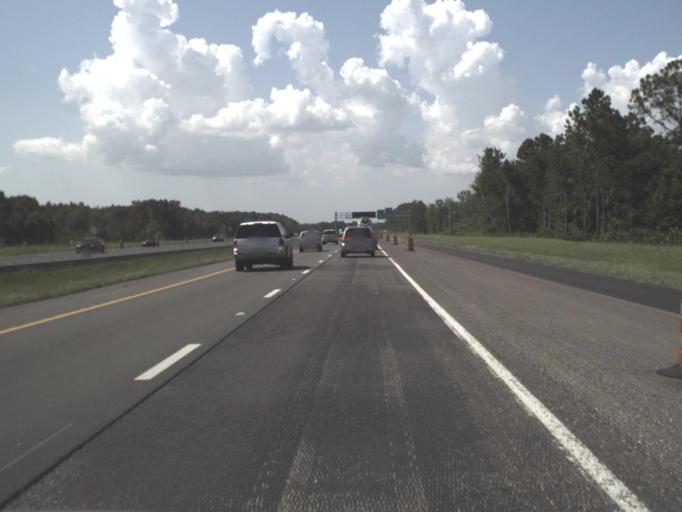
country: US
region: Florida
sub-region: Hillsborough County
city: Pebble Creek
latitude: 28.1478
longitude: -82.3857
